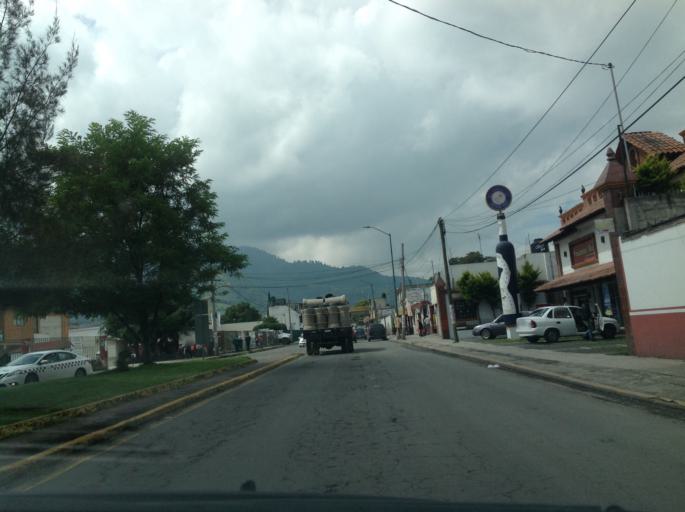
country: MX
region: Morelos
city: Tenango de Arista
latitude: 19.1052
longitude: -99.5867
